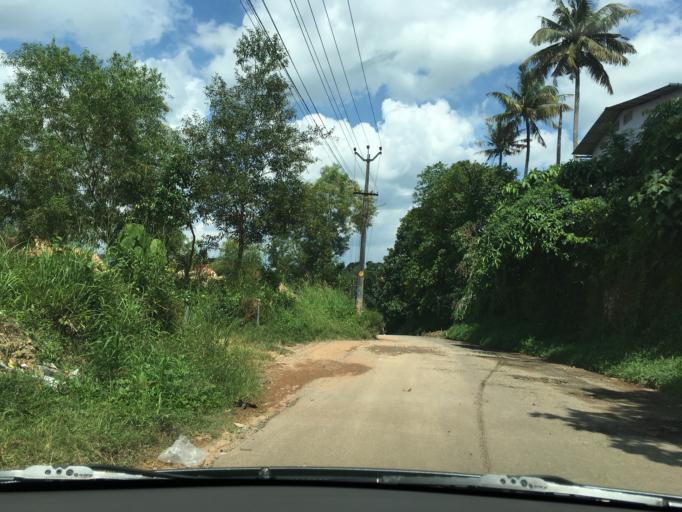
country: IN
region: Kerala
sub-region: Thiruvananthapuram
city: Nedumangad
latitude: 8.6079
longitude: 76.9962
